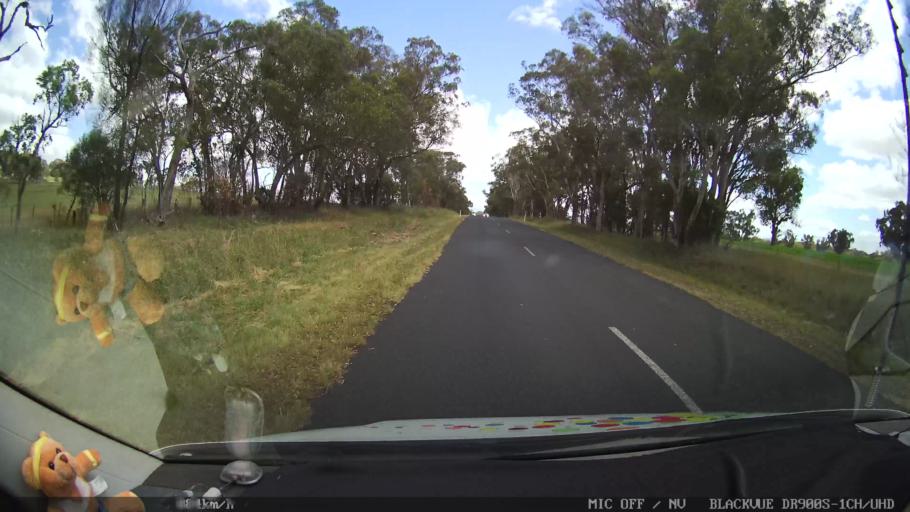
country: AU
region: New South Wales
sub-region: Glen Innes Severn
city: Glen Innes
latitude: -29.4799
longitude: 151.6829
